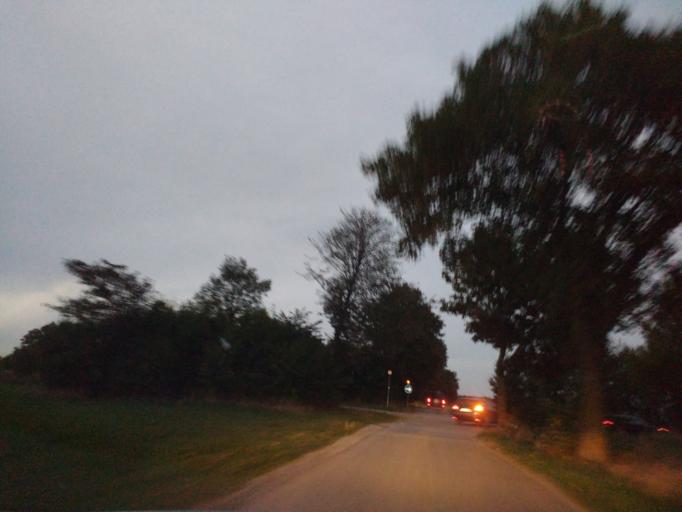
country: DE
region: North Rhine-Westphalia
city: Warstein
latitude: 51.4353
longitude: 8.3880
